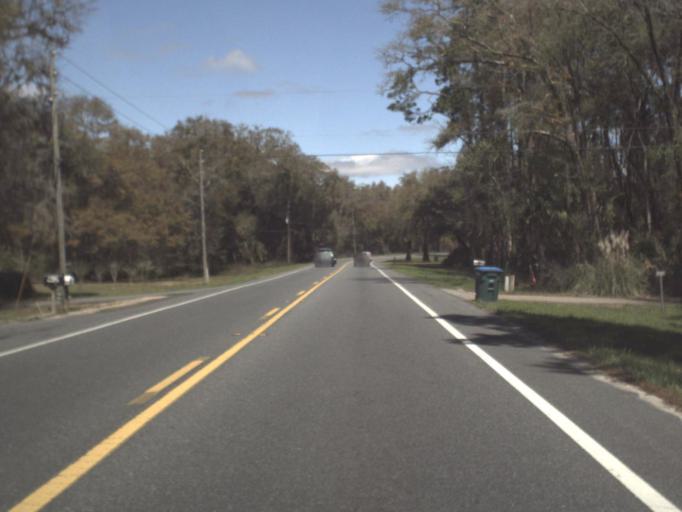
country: US
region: Florida
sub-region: Wakulla County
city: Crawfordville
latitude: 30.0943
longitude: -84.3856
